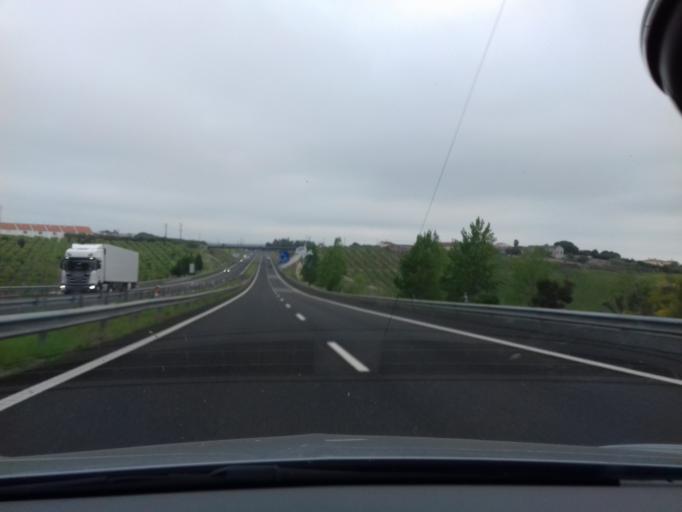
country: PT
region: Leiria
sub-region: Bombarral
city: Bombarral
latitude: 39.2459
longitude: -9.1677
